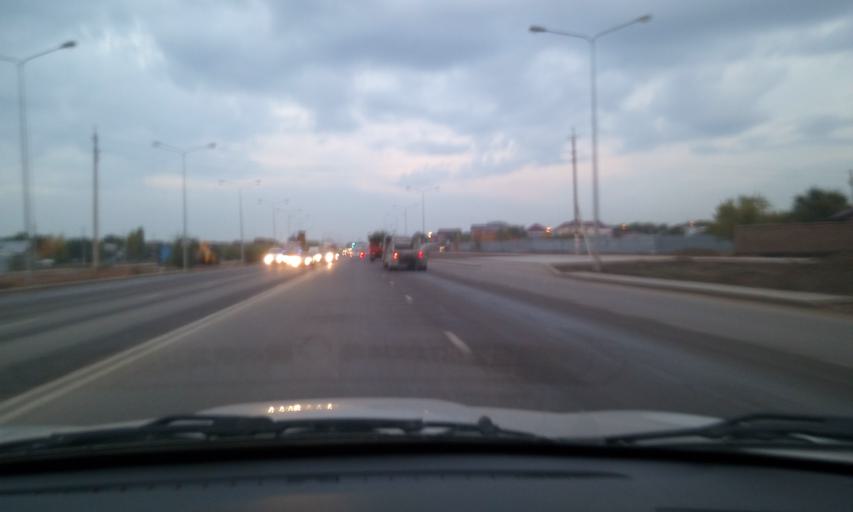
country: KZ
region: Astana Qalasy
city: Astana
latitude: 51.1325
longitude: 71.5096
